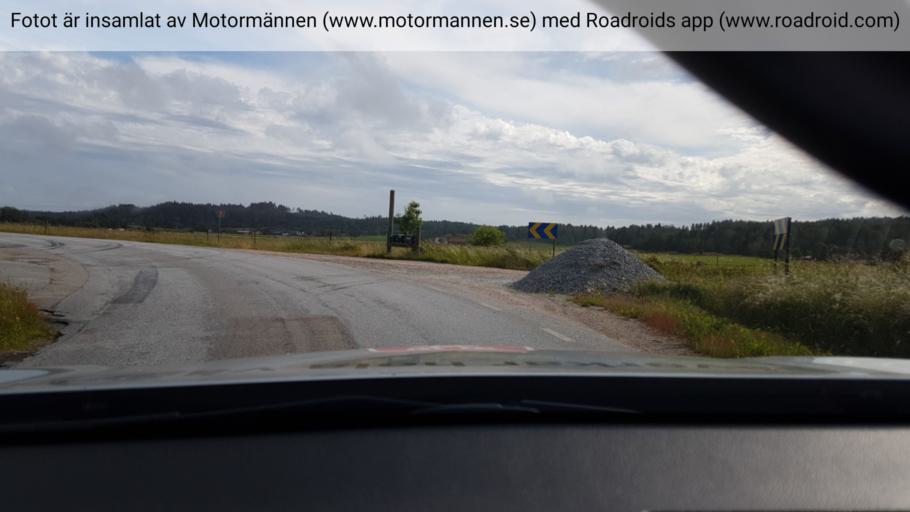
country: SE
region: Vaestra Goetaland
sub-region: Orust
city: Henan
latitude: 58.1708
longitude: 11.7068
